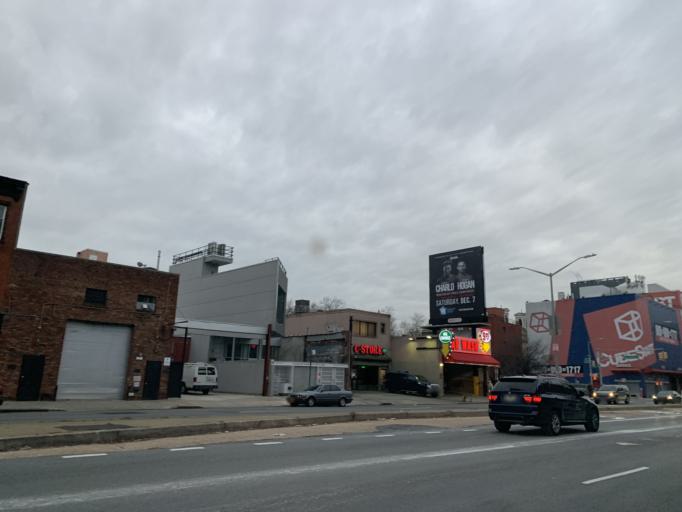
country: US
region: New York
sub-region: Kings County
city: Brooklyn
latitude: 40.6810
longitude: -73.9634
